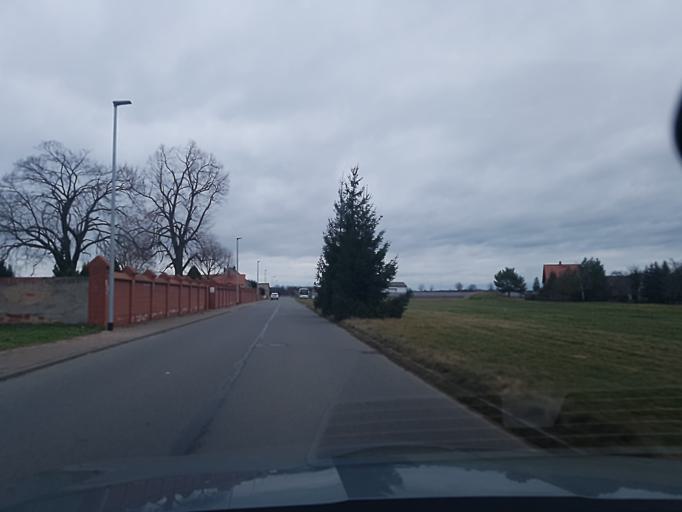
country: DE
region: Brandenburg
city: Falkenberg
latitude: 51.5945
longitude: 13.2946
